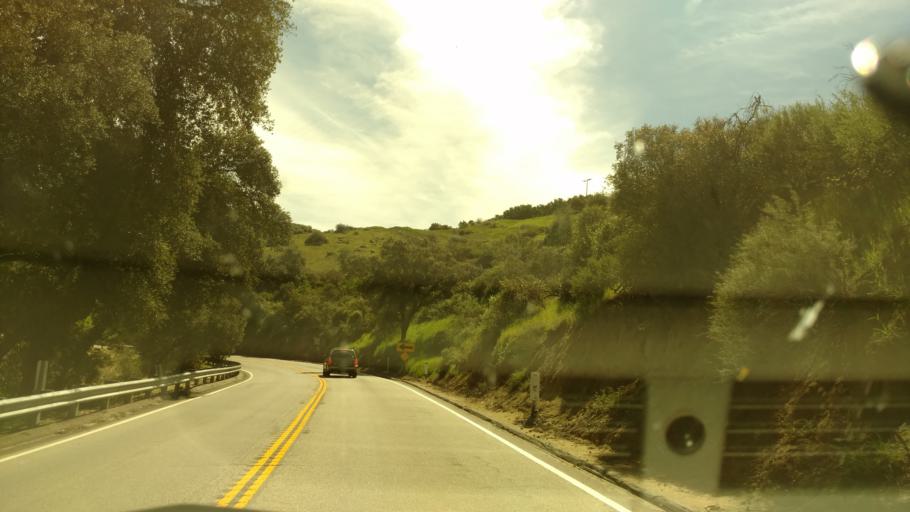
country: US
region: California
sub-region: San Diego County
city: Ramona
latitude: 33.0730
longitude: -116.9026
